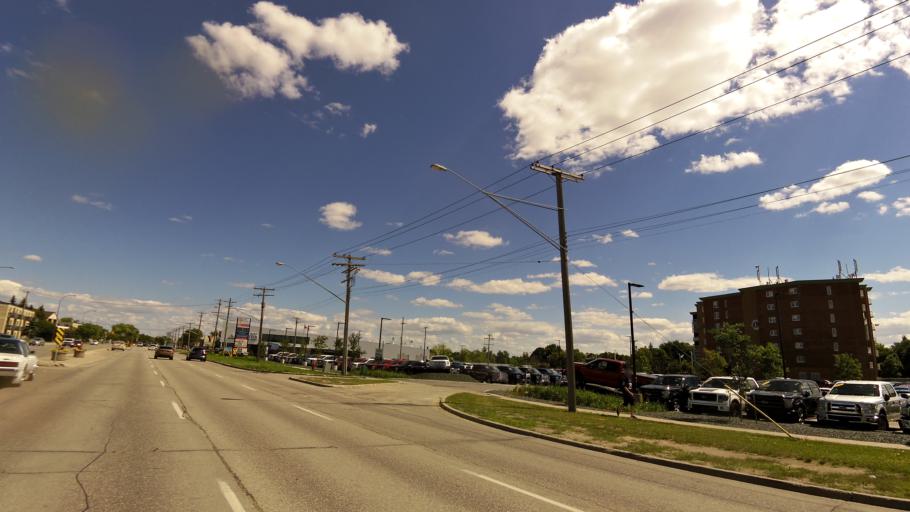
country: CA
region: Manitoba
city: Headingley
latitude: 49.8822
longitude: -97.3116
